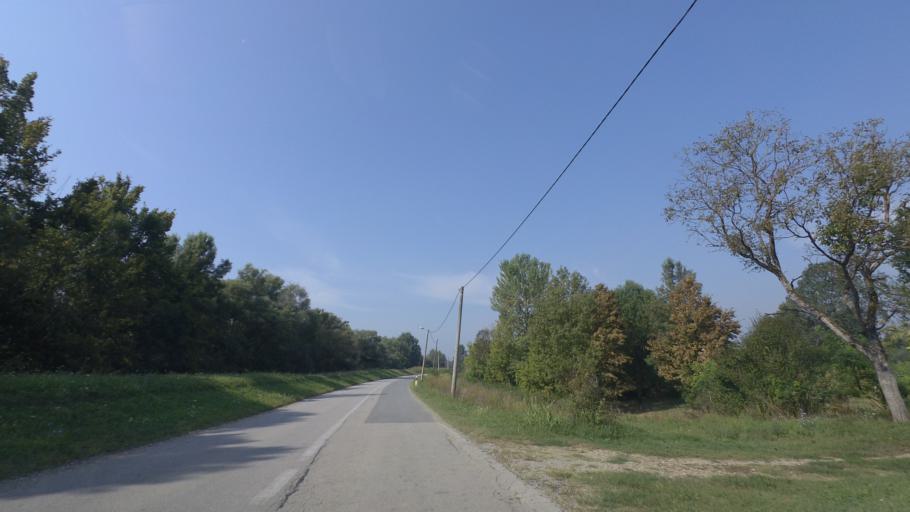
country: BA
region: Republika Srpska
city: Bosanska Dubica
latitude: 45.2412
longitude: 16.8682
